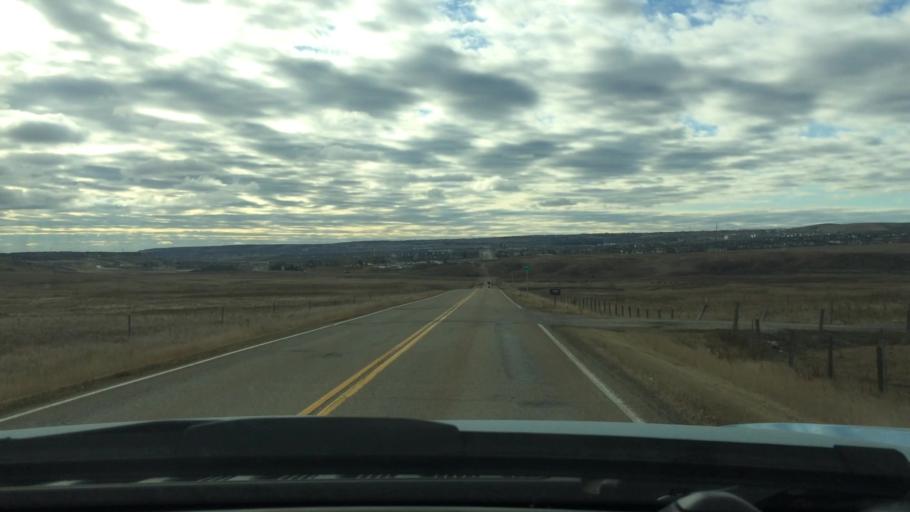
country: CA
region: Alberta
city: Airdrie
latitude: 51.1977
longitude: -114.1412
